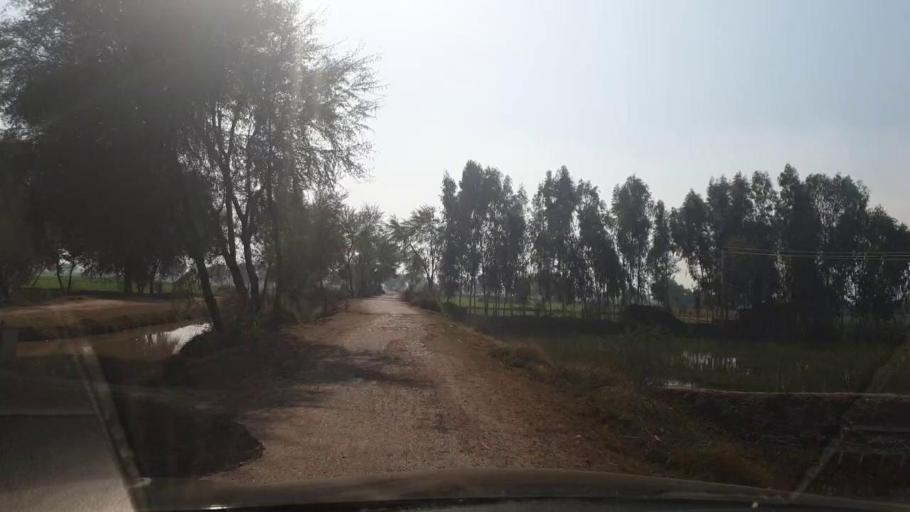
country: PK
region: Sindh
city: Khairpur
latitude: 28.1332
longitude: 69.6475
